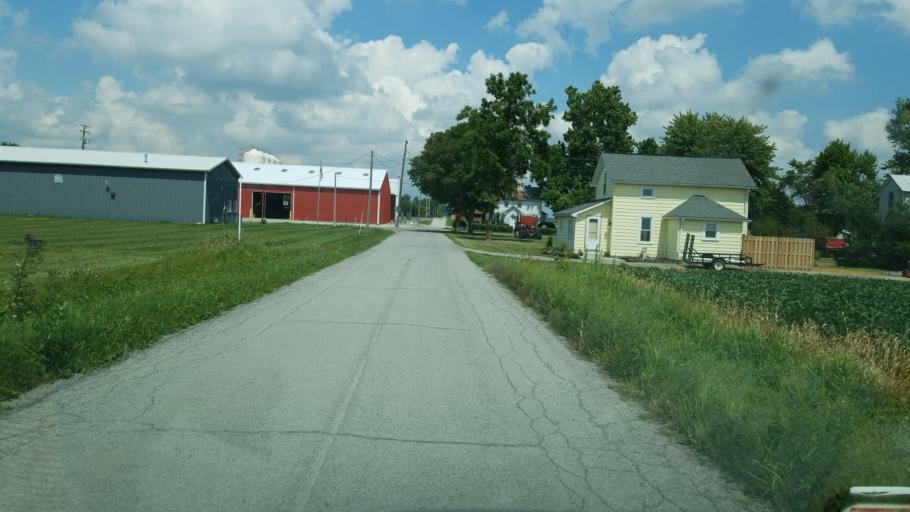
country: US
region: Ohio
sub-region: Crawford County
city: Bucyrus
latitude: 40.7168
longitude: -83.0381
